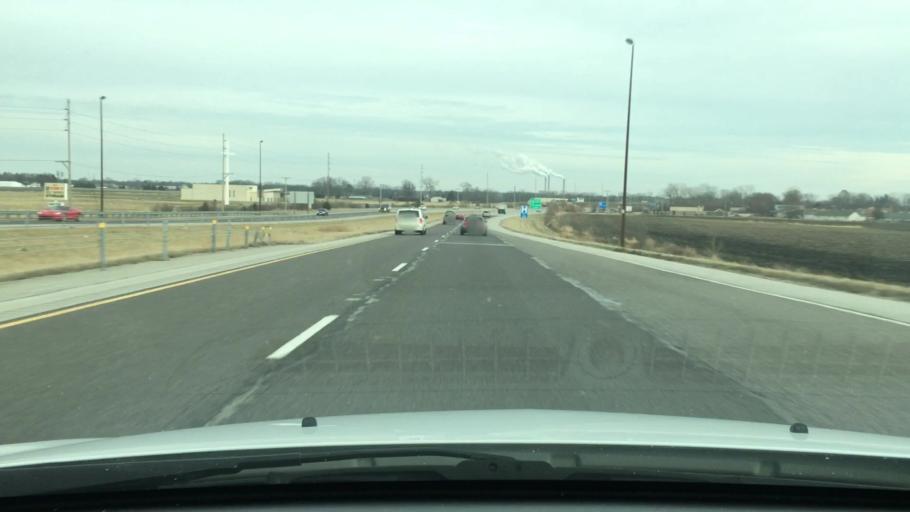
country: US
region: Illinois
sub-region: Sangamon County
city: Southern View
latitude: 39.7413
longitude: -89.6644
